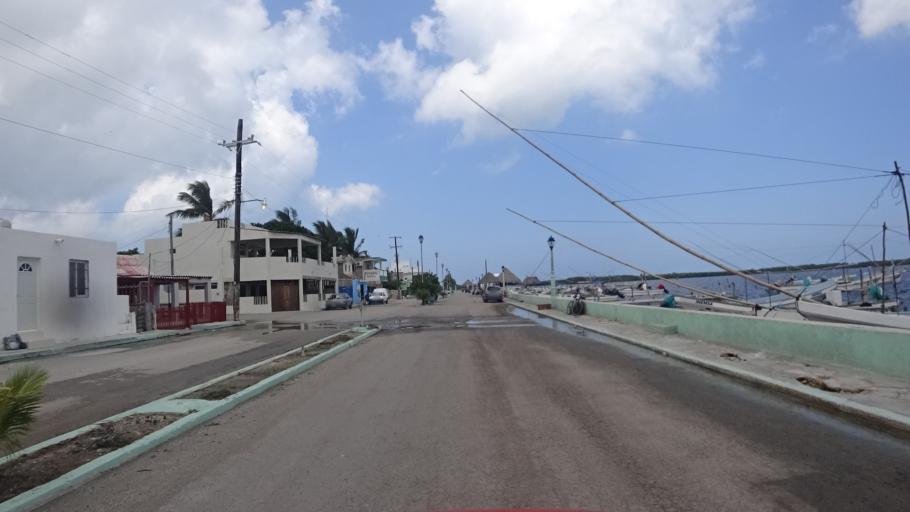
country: MX
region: Yucatan
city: Rio Lagartos
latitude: 21.5978
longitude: -88.1562
